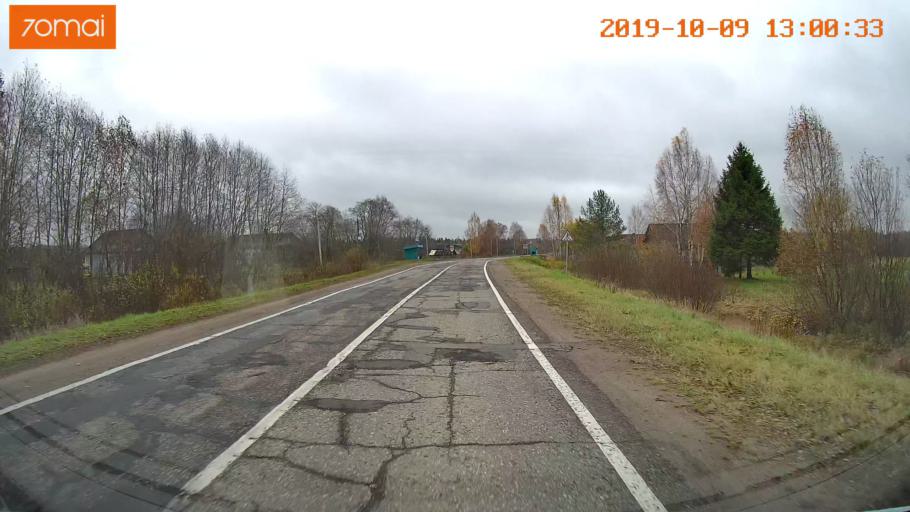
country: RU
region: Jaroslavl
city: Prechistoye
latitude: 58.3762
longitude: 40.4813
